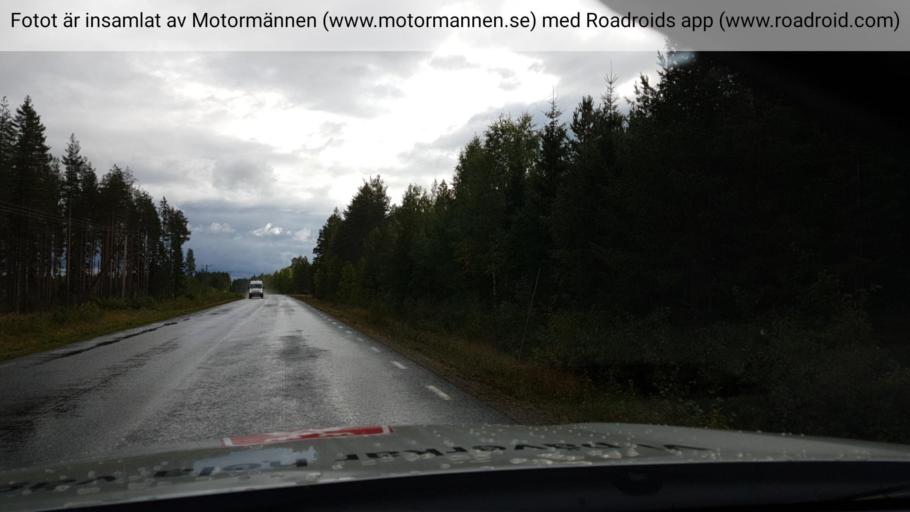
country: SE
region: Norrbotten
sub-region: Bodens Kommun
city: Boden
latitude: 65.8384
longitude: 21.4877
